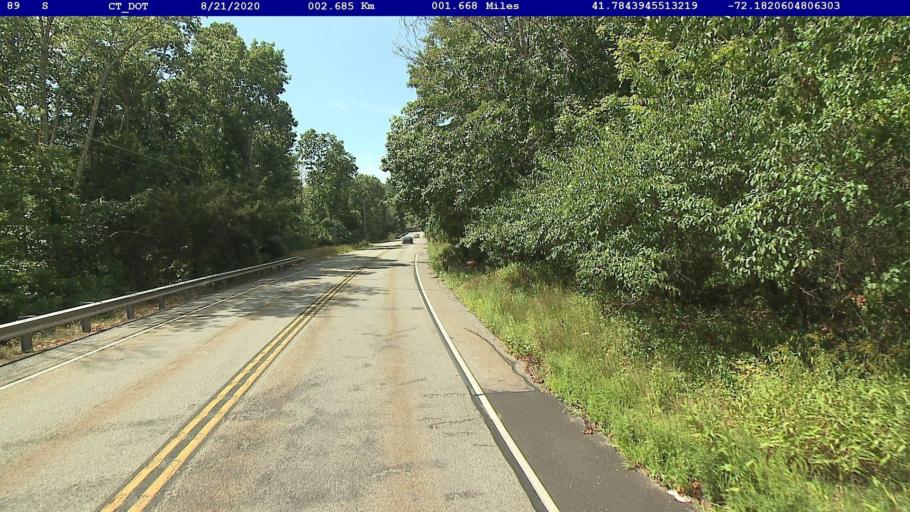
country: US
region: Connecticut
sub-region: Tolland County
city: Mansfield City
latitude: 41.7844
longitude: -72.1821
